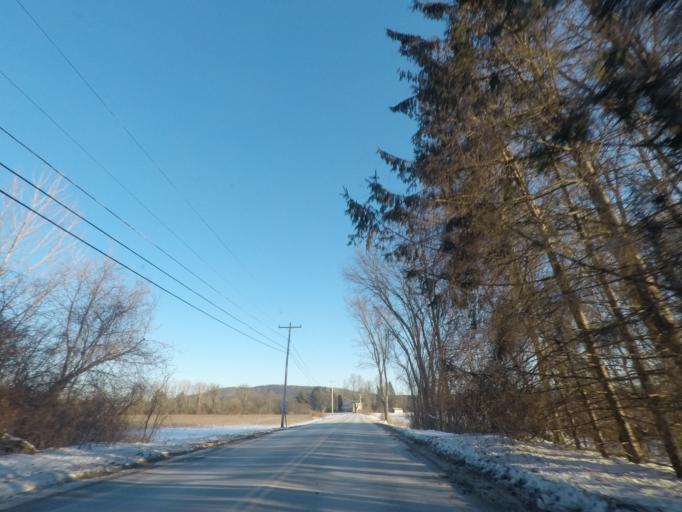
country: US
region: New York
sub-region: Saratoga County
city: Waterford
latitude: 42.8303
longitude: -73.6493
